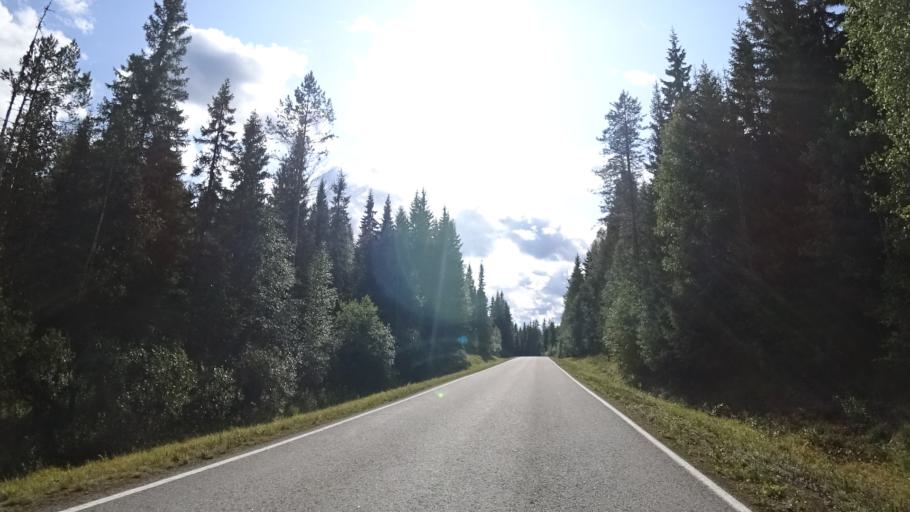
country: RU
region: Republic of Karelia
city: Vyartsilya
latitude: 62.2443
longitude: 30.7119
